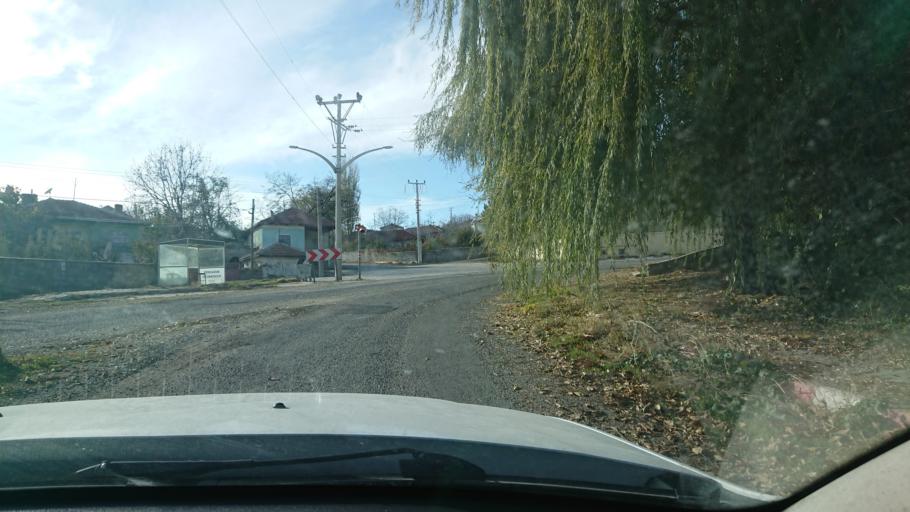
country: TR
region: Aksaray
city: Sariyahsi
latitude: 38.9592
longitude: 33.8862
